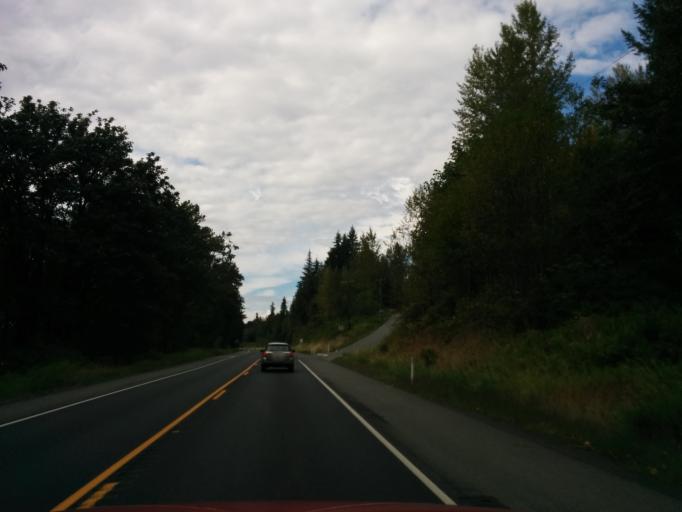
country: US
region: Washington
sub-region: King County
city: Duvall
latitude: 47.7821
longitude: -121.9668
